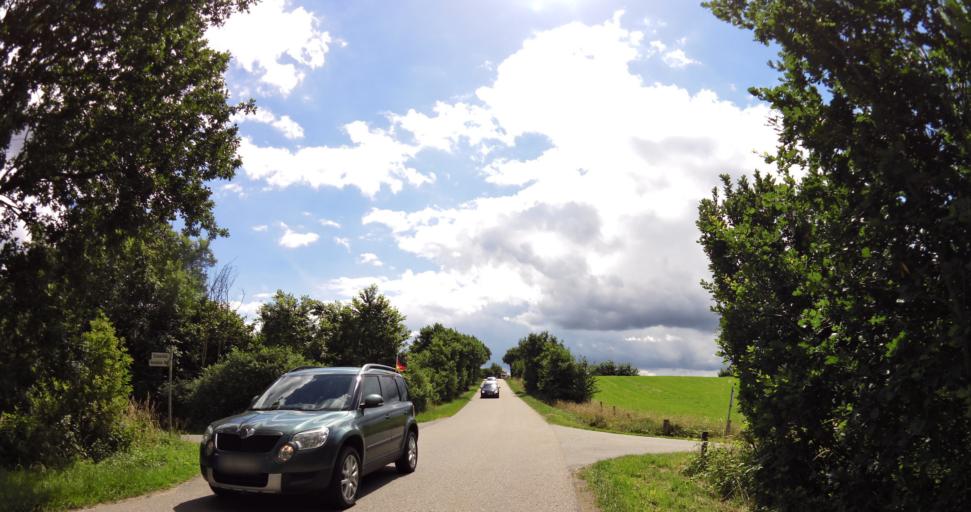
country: DE
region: Schleswig-Holstein
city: Hummelfeld
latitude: 54.4920
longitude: 9.7289
